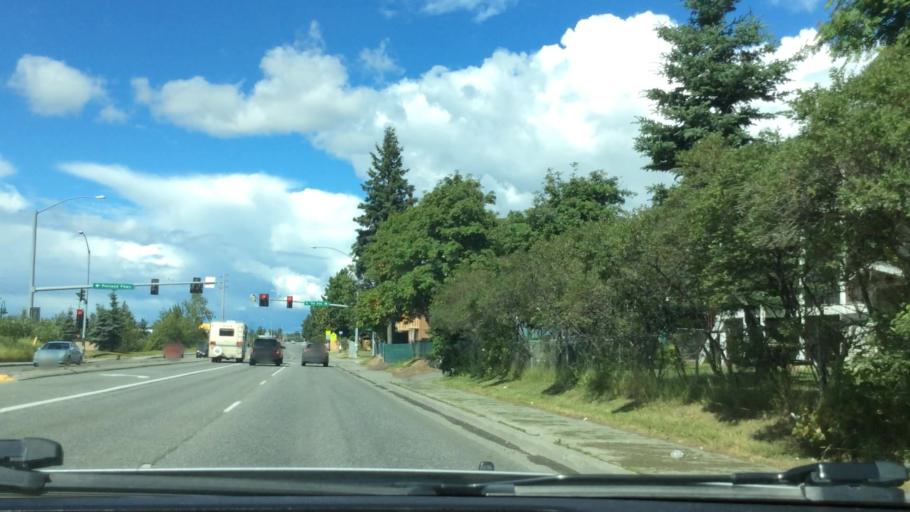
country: US
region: Alaska
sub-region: Anchorage Municipality
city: Anchorage
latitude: 61.2151
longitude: -149.8082
